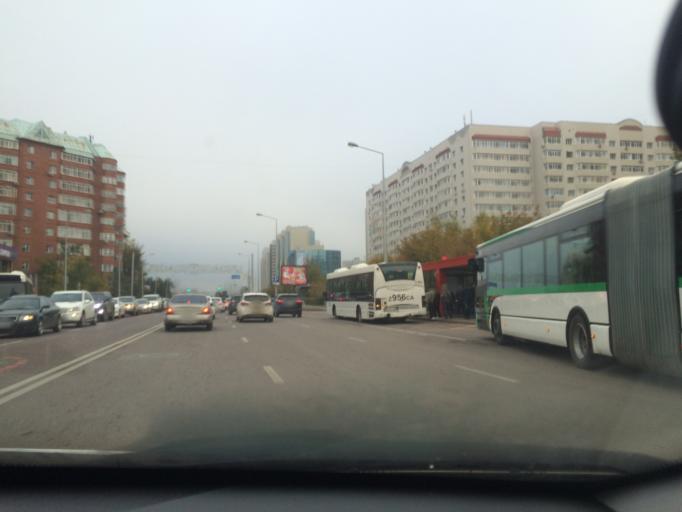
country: KZ
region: Astana Qalasy
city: Astana
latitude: 51.1655
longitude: 71.4089
